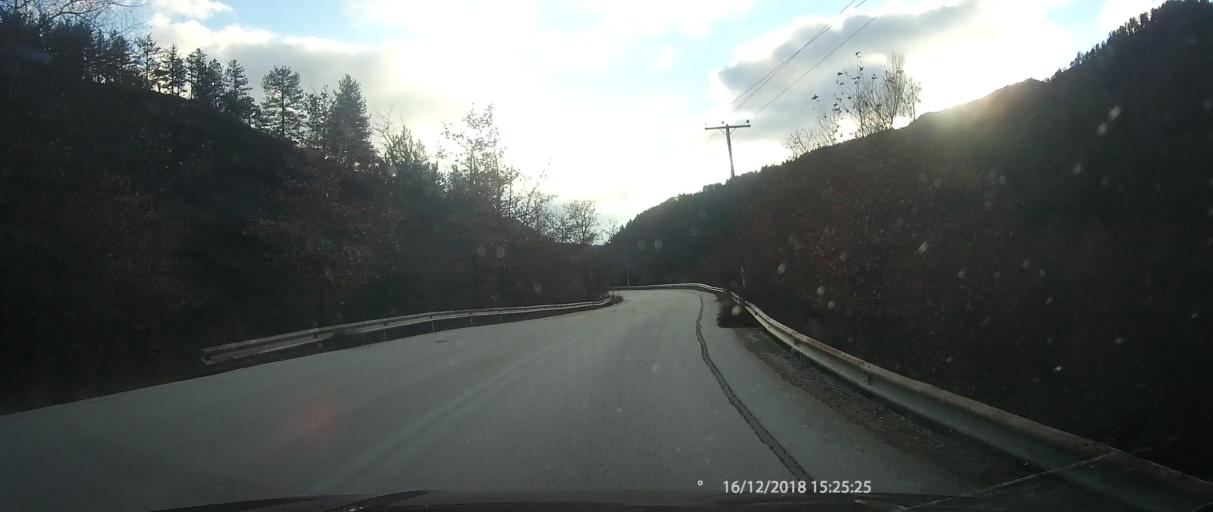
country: GR
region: Epirus
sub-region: Nomos Ioanninon
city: Konitsa
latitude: 40.1283
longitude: 20.7827
